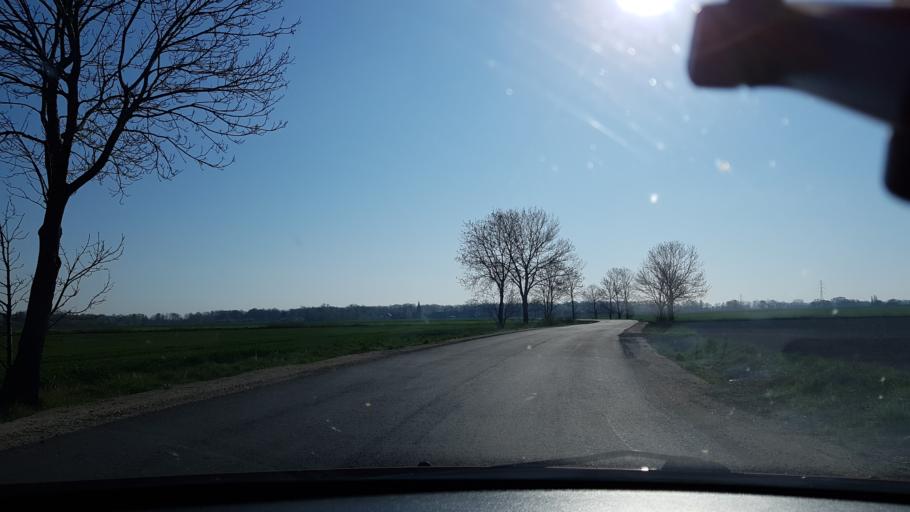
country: CZ
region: Olomoucky
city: Vidnava
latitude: 50.4267
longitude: 17.2424
